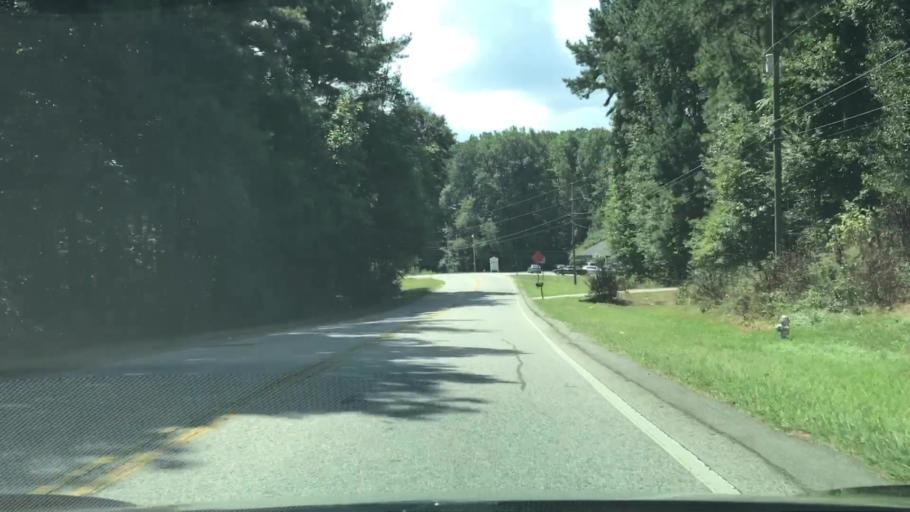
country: US
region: Georgia
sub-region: Gwinnett County
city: Snellville
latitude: 33.8590
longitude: -84.0482
